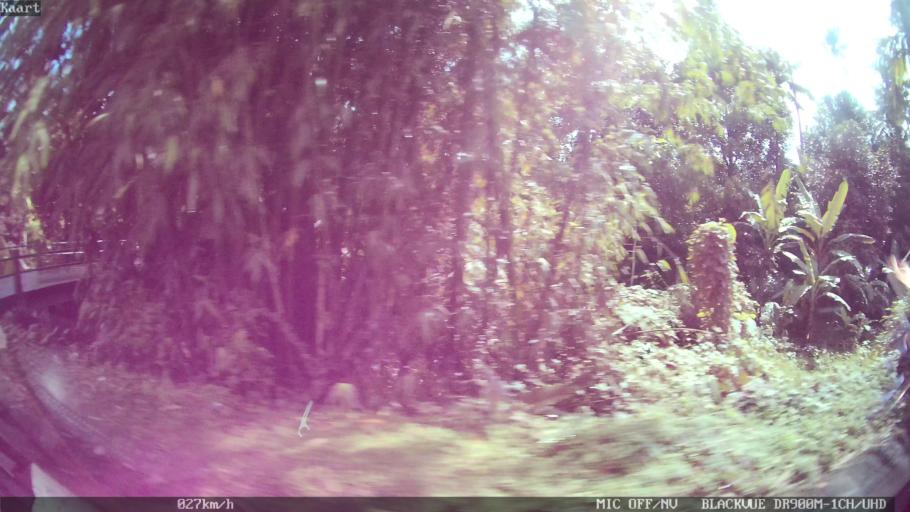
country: ID
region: Bali
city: Banjar Tebongkang
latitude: -8.5454
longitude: 115.2562
